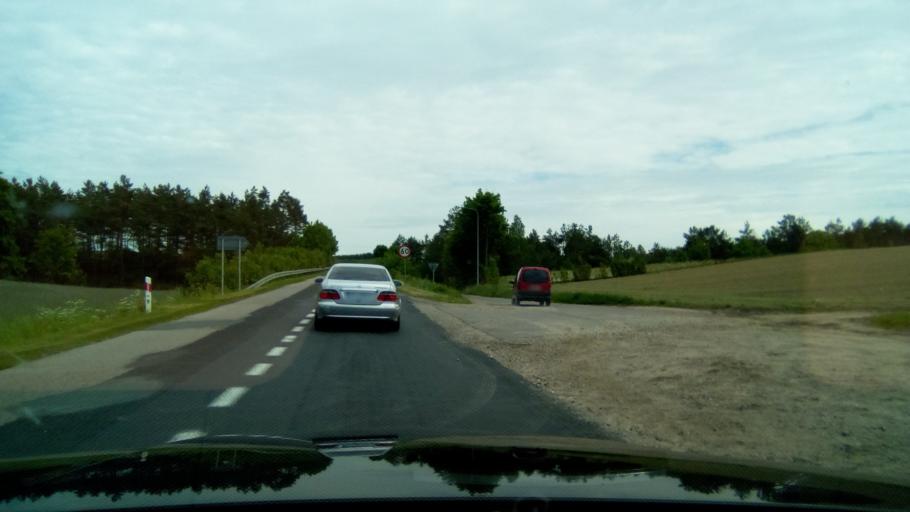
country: PL
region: Pomeranian Voivodeship
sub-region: Powiat bytowski
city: Lipnica
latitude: 54.0594
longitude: 17.4251
